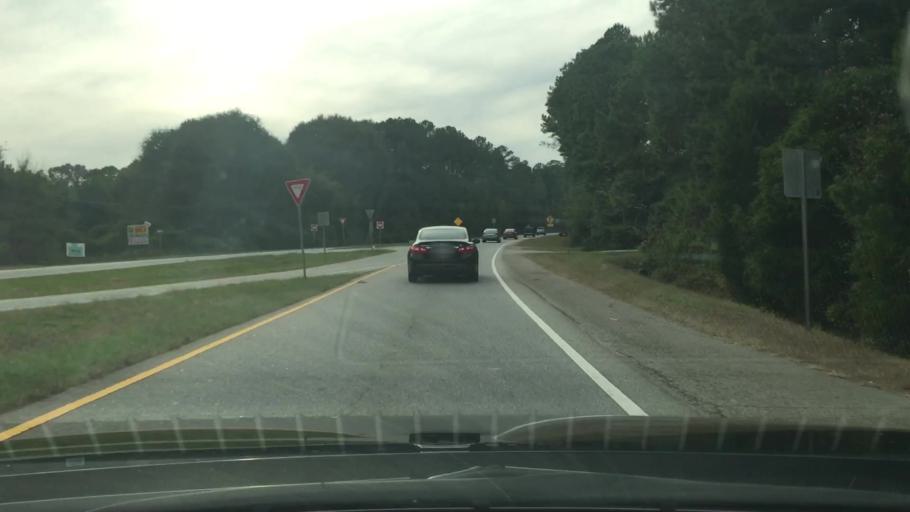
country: US
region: Georgia
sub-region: Spalding County
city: Experiment
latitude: 33.2393
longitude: -84.3208
